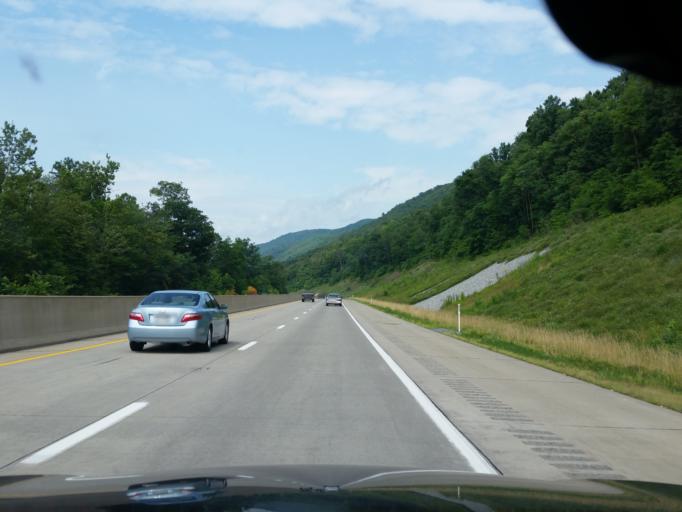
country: US
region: Pennsylvania
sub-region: Juniata County
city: Mifflintown
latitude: 40.6114
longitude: -77.4484
